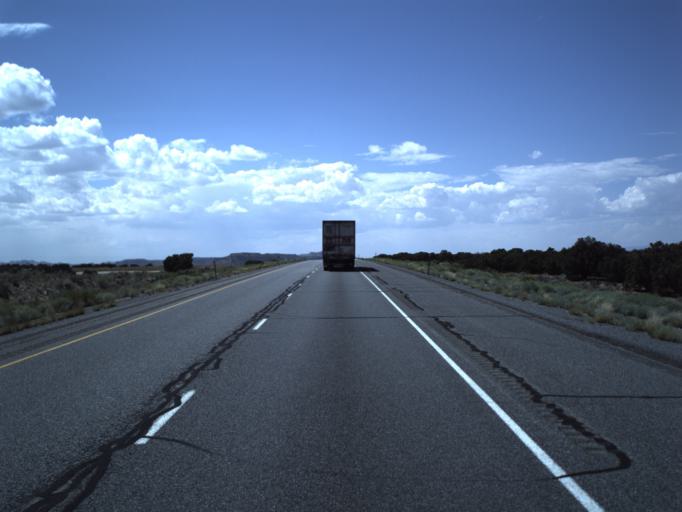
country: US
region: Utah
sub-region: Emery County
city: Castle Dale
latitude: 38.8979
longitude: -110.5838
